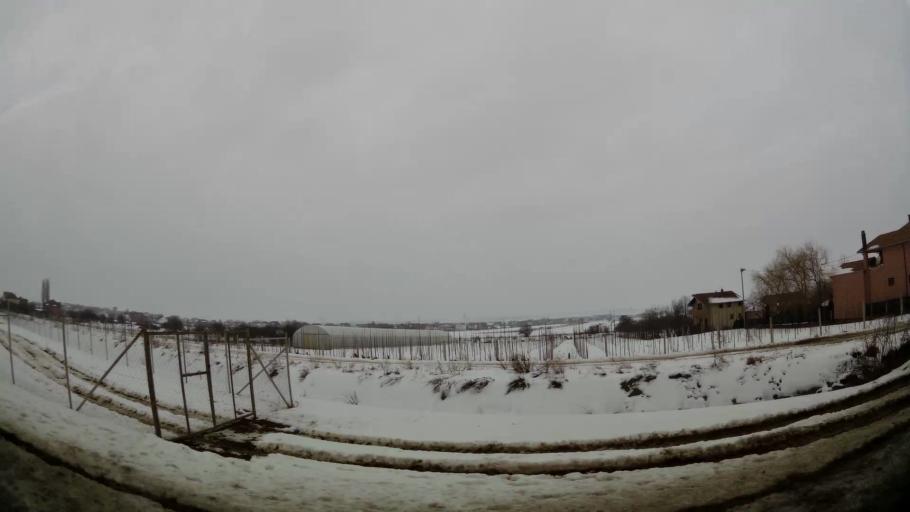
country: XK
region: Pristina
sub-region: Komuna e Prishtines
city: Pristina
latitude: 42.7256
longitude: 21.1447
